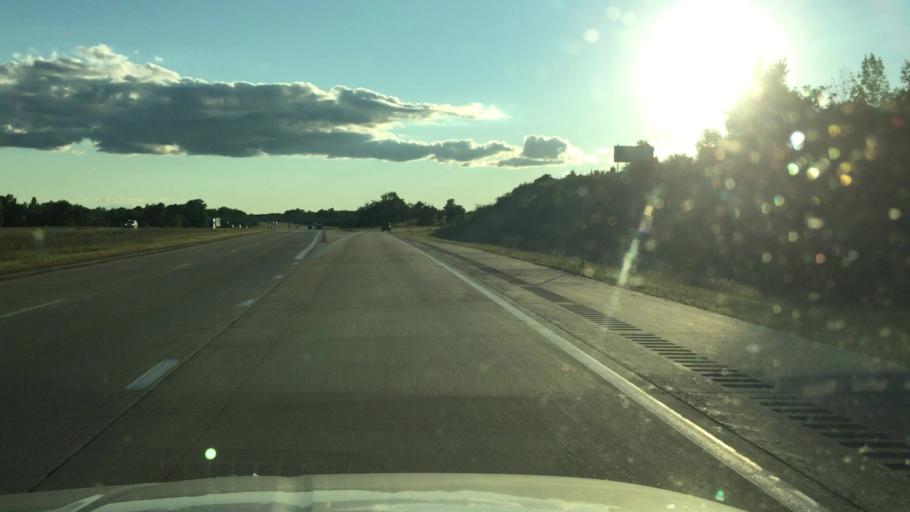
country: US
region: Michigan
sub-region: Lapeer County
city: Lapeer
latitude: 43.0318
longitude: -83.3540
